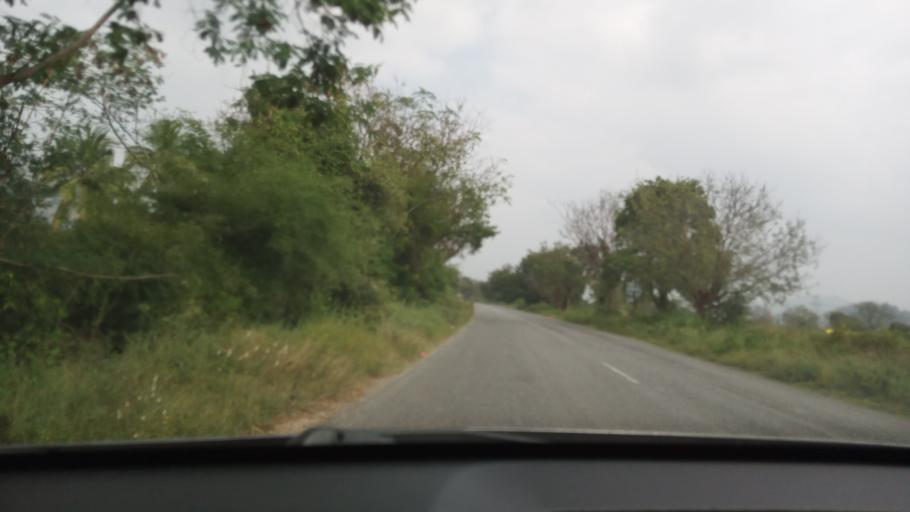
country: IN
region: Andhra Pradesh
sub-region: Chittoor
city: Madanapalle
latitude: 13.6521
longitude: 78.8316
